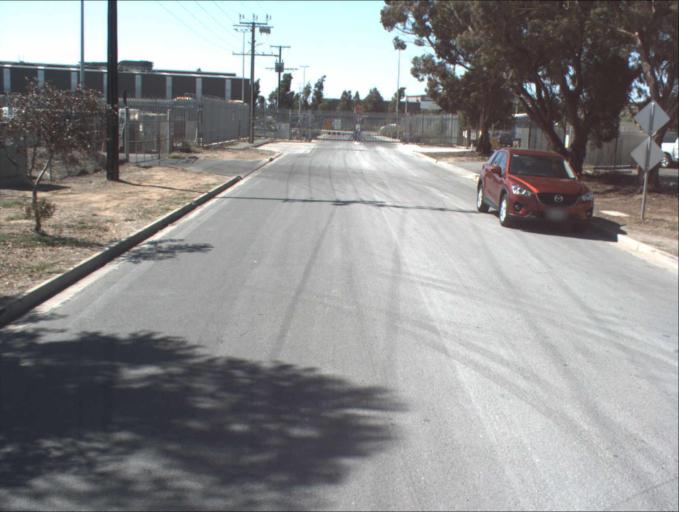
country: AU
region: South Australia
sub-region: Port Adelaide Enfield
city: Enfield
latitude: -34.8339
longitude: 138.5902
